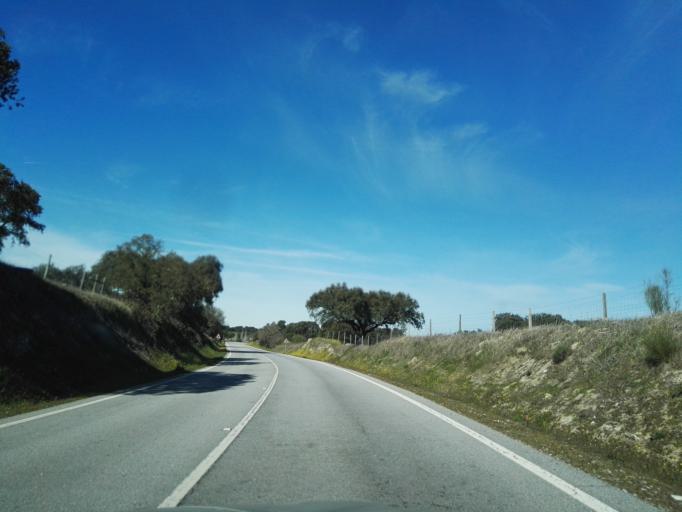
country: PT
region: Portalegre
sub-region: Arronches
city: Arronches
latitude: 39.0633
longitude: -7.2741
